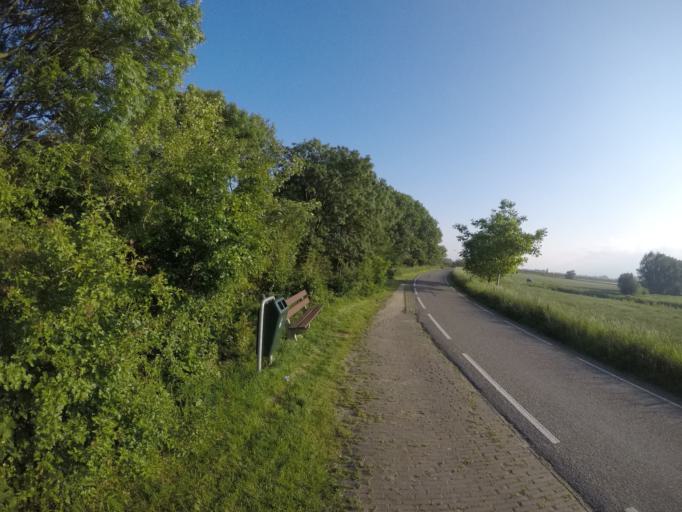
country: NL
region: Gelderland
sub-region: Gemeente Westervoort
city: Westervoort
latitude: 51.9555
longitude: 5.9644
